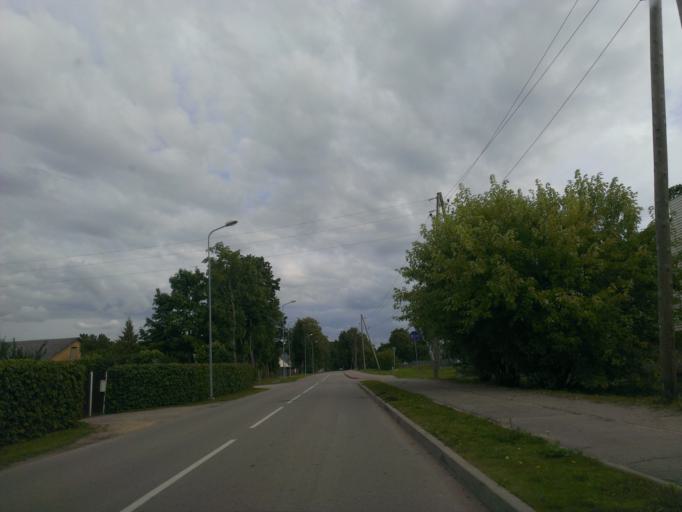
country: LV
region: Ikskile
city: Ikskile
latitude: 56.8322
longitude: 24.4839
